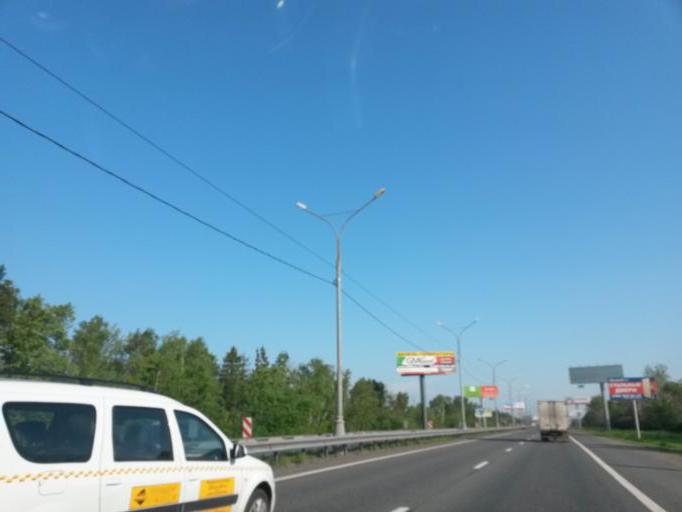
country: RU
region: Moskovskaya
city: Gorki-Leninskiye
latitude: 55.5206
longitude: 37.8231
